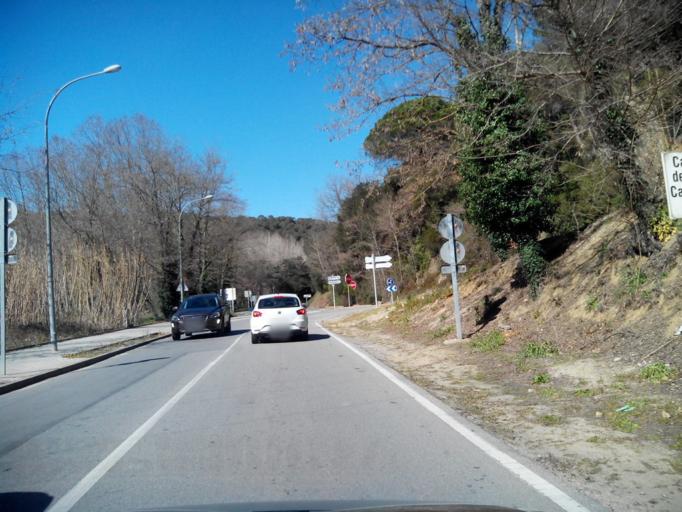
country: ES
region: Catalonia
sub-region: Provincia de Barcelona
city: Dosrius
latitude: 41.5970
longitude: 2.4016
